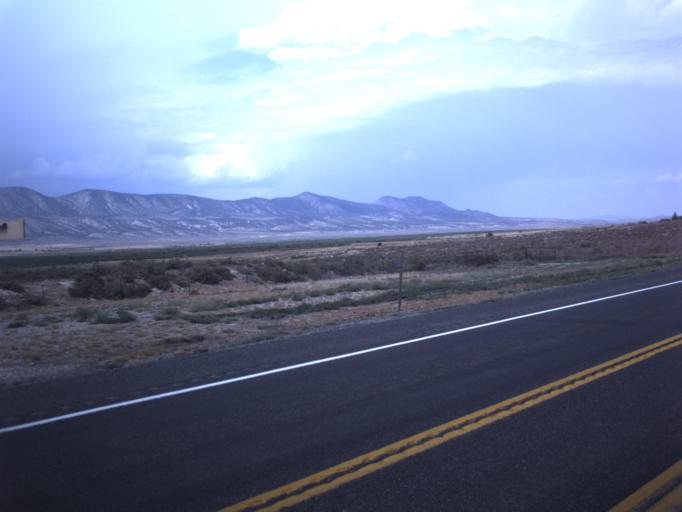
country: US
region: Utah
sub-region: Sanpete County
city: Gunnison
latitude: 39.2065
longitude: -111.8481
